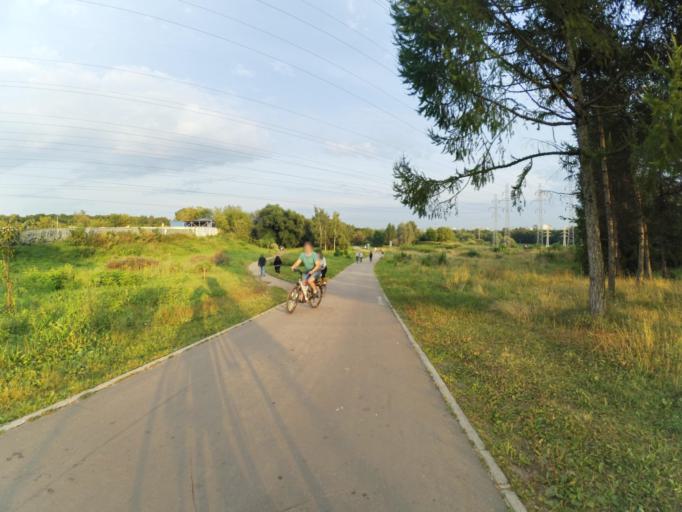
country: RU
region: Moscow
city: Novyye Kuz'minki
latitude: 55.6904
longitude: 37.7571
